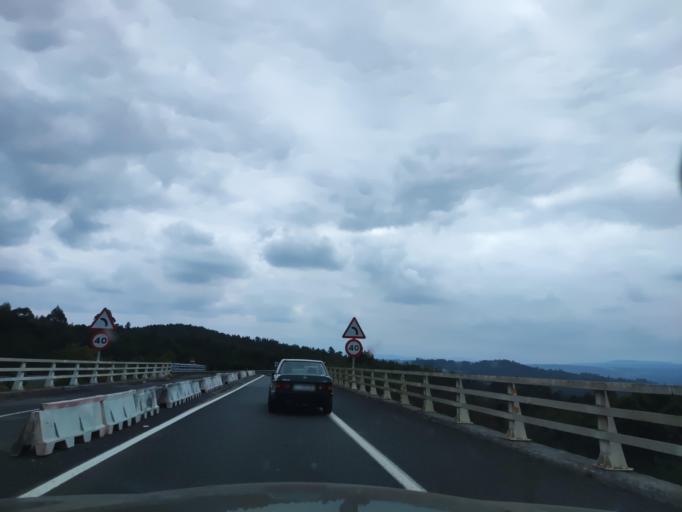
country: ES
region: Galicia
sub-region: Provincia da Coruna
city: Teo
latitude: 42.7871
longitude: -8.5474
